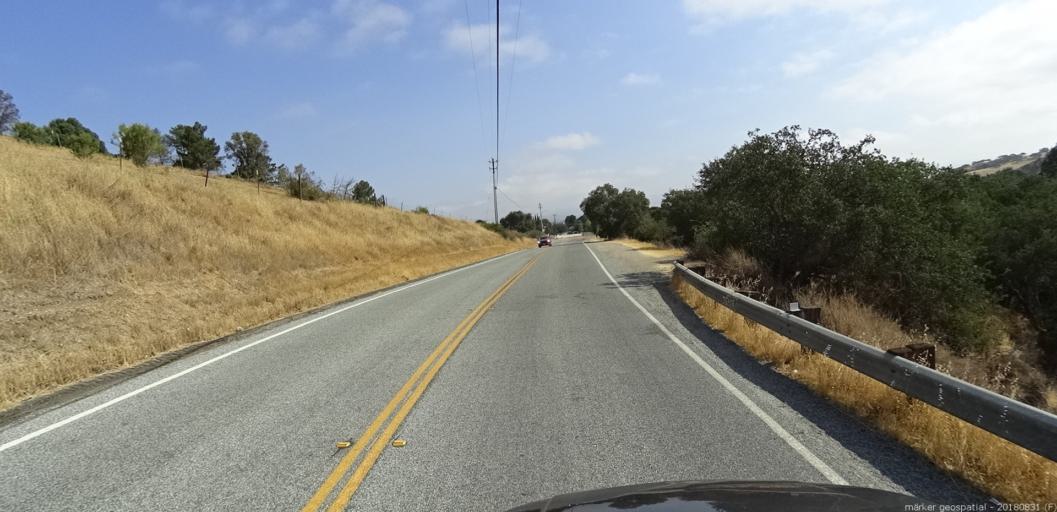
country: US
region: California
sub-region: Monterey County
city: King City
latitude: 36.1789
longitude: -121.1530
